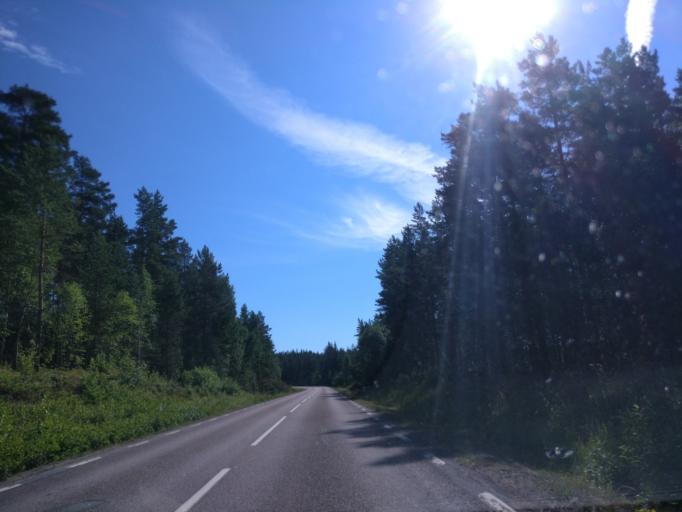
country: SE
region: Vaermland
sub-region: Filipstads Kommun
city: Lesjofors
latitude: 60.0432
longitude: 13.9412
